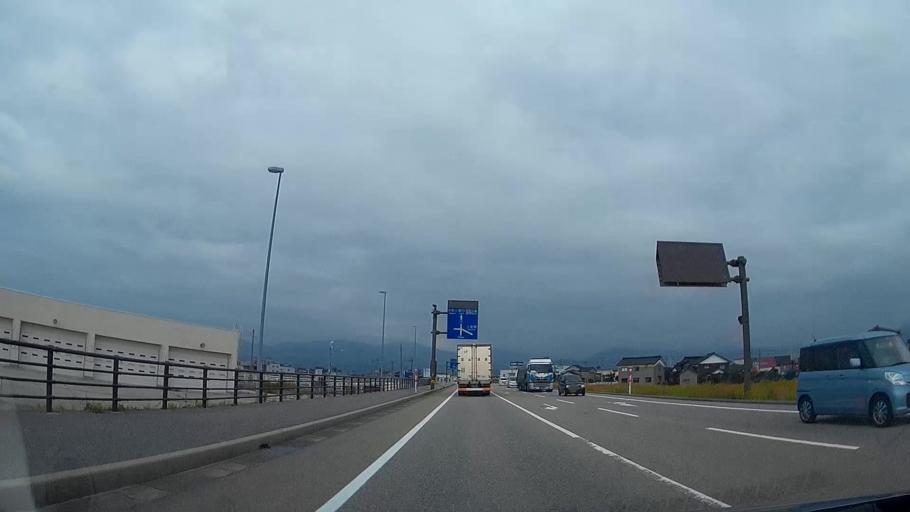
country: JP
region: Toyama
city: Nyuzen
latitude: 36.9266
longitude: 137.4882
